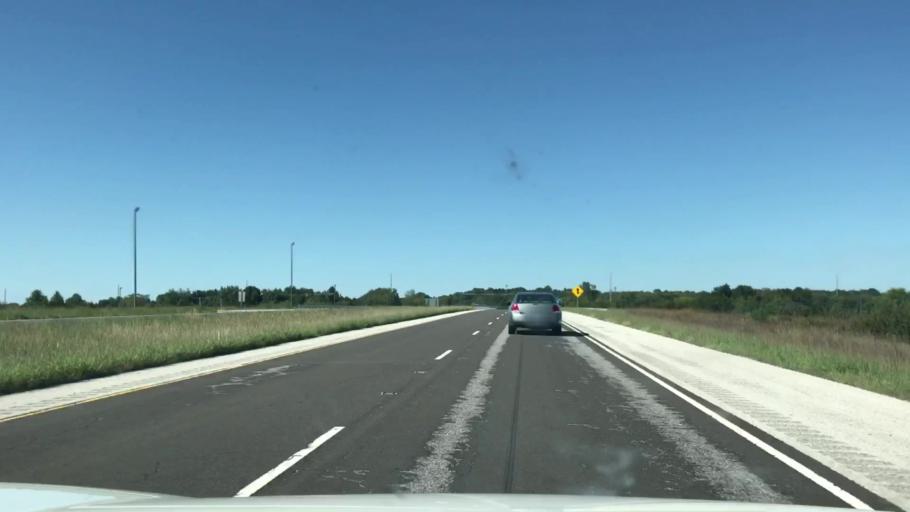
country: US
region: Illinois
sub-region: Madison County
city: South Roxana
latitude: 38.8309
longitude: -90.0436
